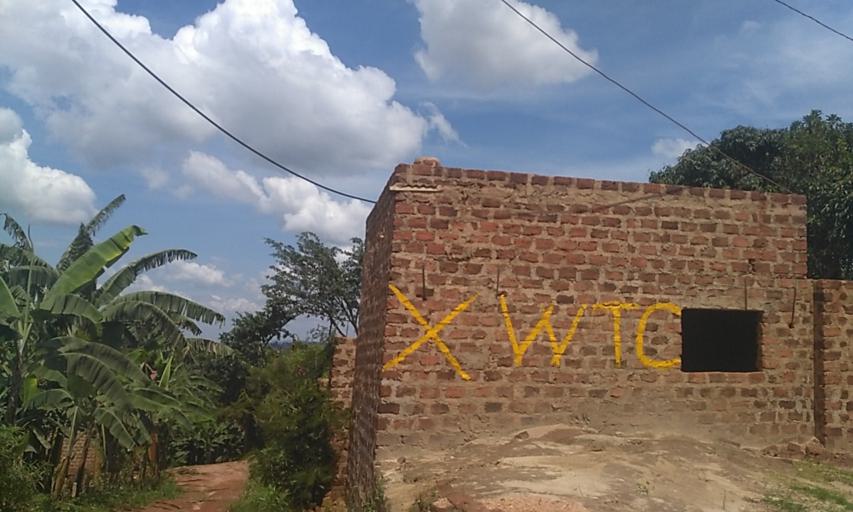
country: UG
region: Central Region
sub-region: Wakiso District
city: Wakiso
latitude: 0.3945
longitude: 32.4617
